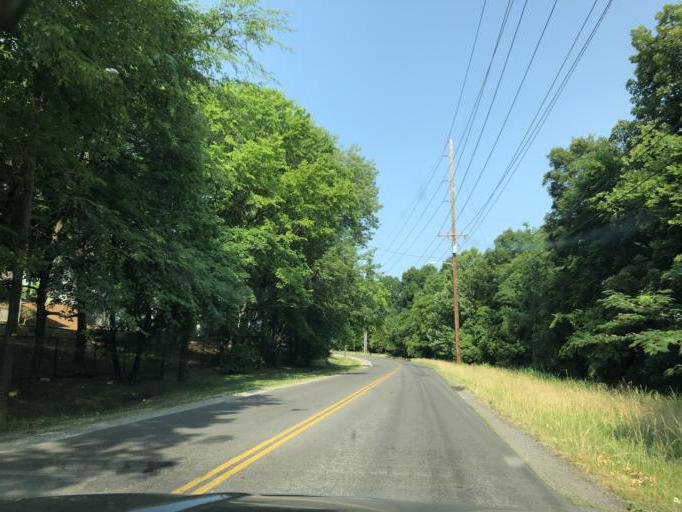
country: US
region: Tennessee
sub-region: Rutherford County
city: La Vergne
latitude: 36.0552
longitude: -86.6388
